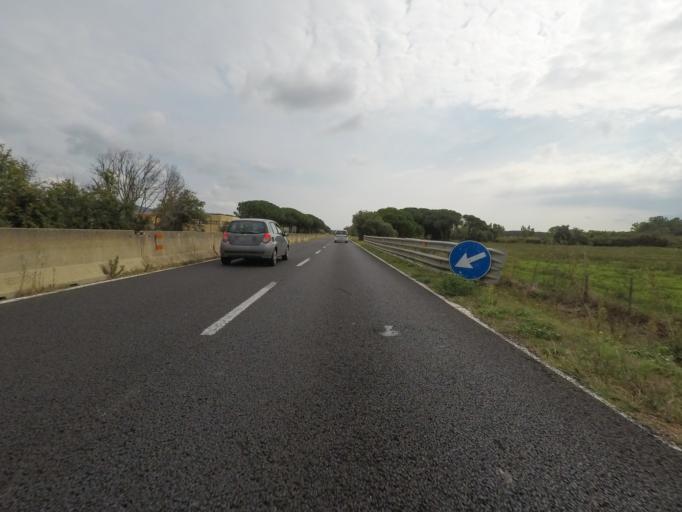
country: IT
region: Tuscany
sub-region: Provincia di Grosseto
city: Albinia
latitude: 42.4898
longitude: 11.2133
